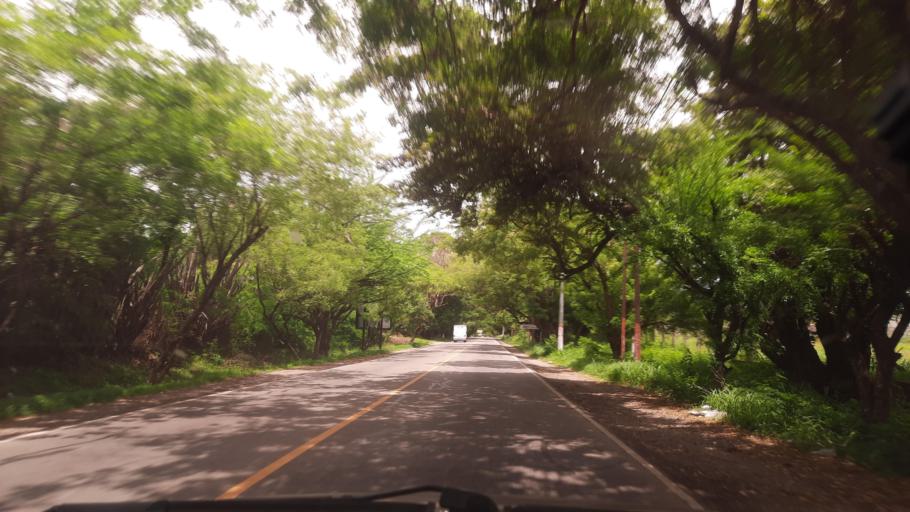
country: GT
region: Zacapa
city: Estanzuela
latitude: 14.9876
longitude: -89.5621
